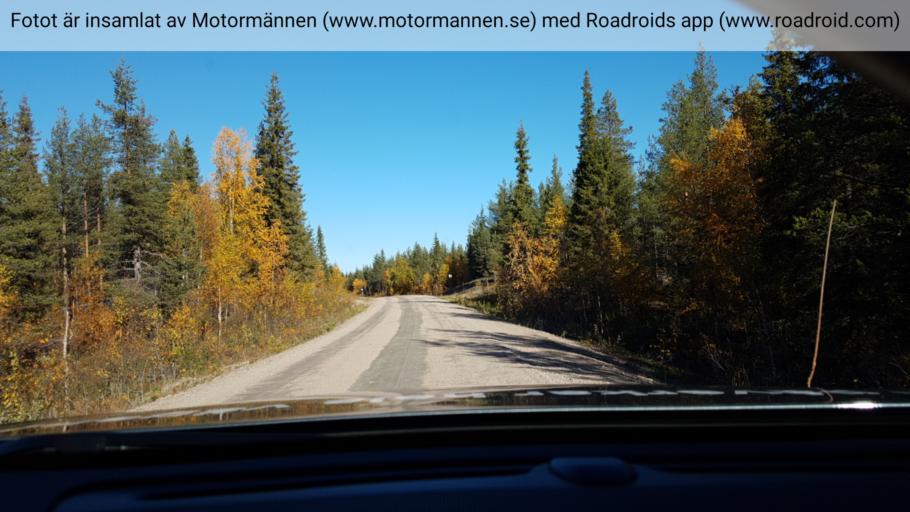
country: SE
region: Norrbotten
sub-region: Gallivare Kommun
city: Gaellivare
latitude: 66.6992
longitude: 20.8909
